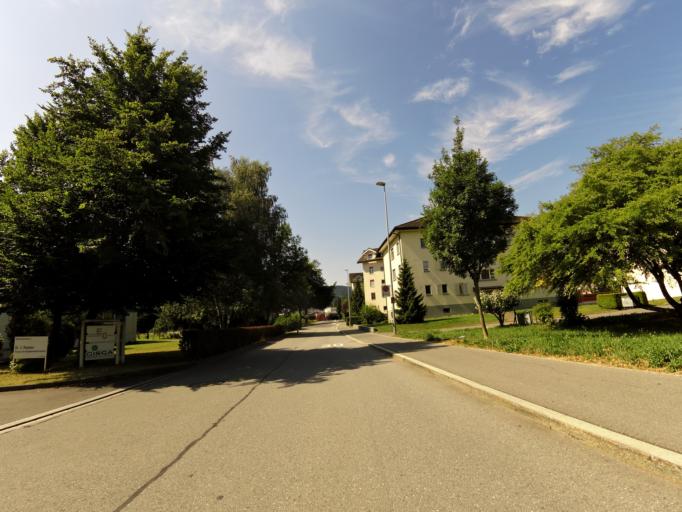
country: CH
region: Lucerne
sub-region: Lucerne-Land District
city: Meierskappel
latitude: 47.1440
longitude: 8.4328
